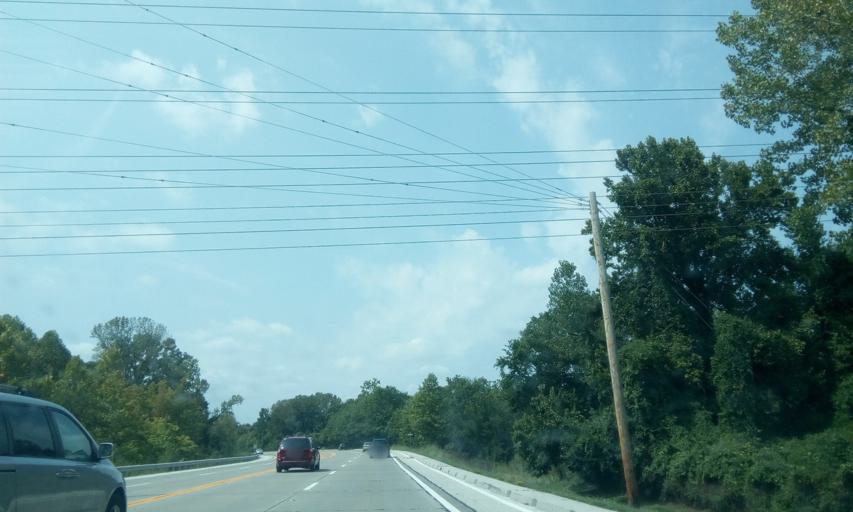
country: US
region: Missouri
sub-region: Saint Louis County
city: Town and Country
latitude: 38.5800
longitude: -90.4583
